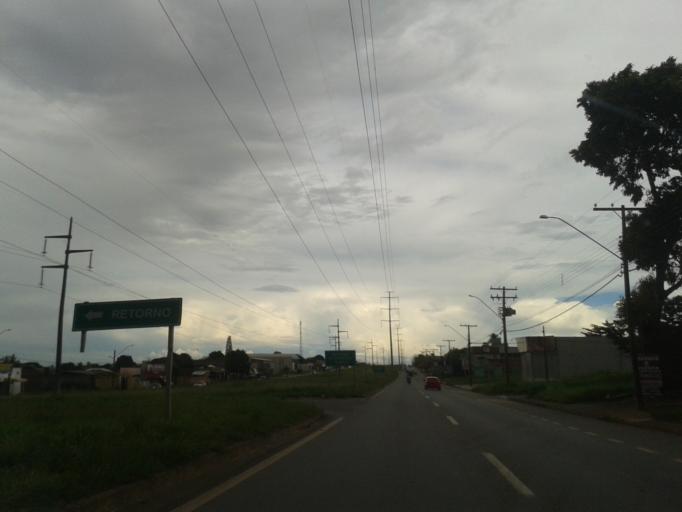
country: BR
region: Goias
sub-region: Aparecida De Goiania
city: Aparecida de Goiania
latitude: -16.7801
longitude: -49.2867
